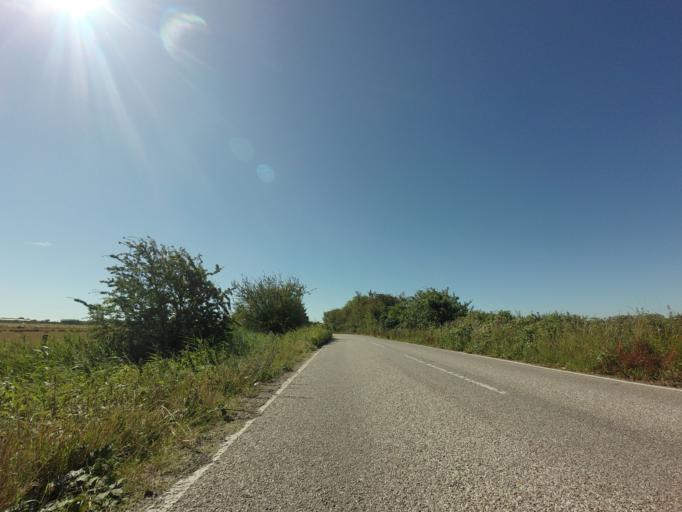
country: GB
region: England
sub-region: Kent
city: Ash
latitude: 51.3194
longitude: 1.2147
